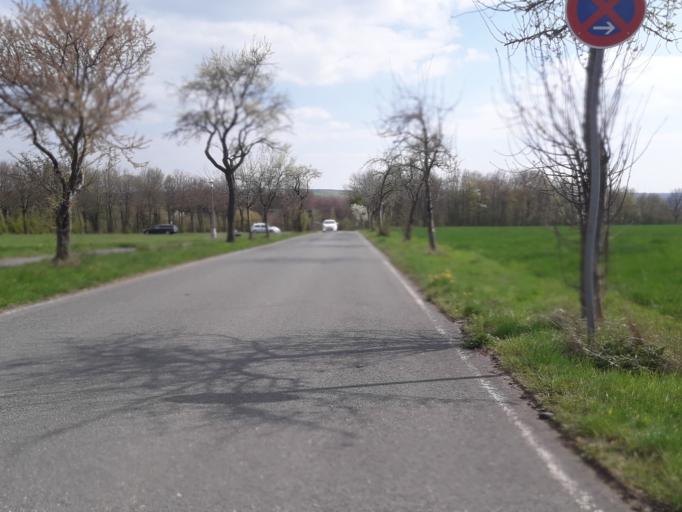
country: DE
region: North Rhine-Westphalia
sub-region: Regierungsbezirk Detmold
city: Paderborn
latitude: 51.6872
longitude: 8.7779
